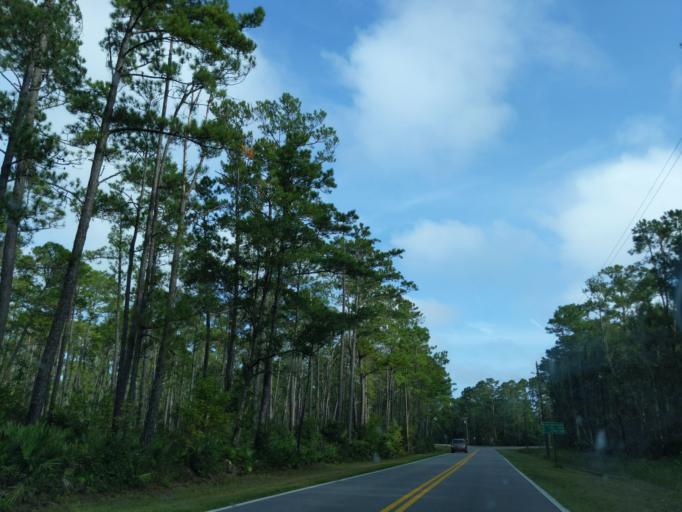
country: US
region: Florida
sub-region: Wakulla County
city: Crawfordville
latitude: 30.1033
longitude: -84.3060
